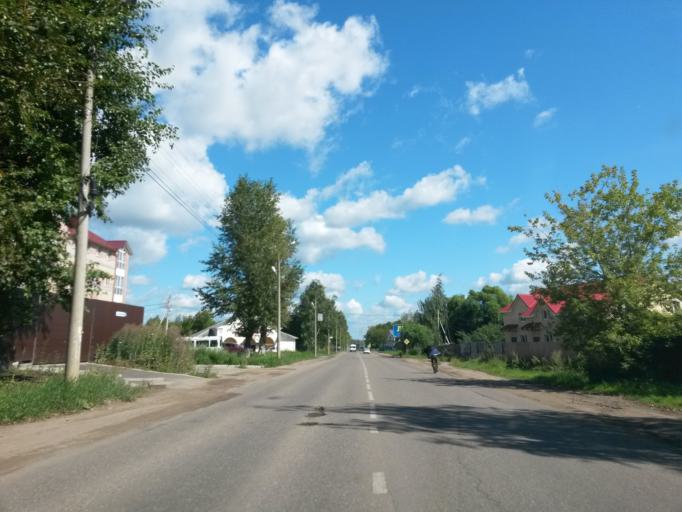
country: RU
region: Jaroslavl
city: Yaroslavl
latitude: 57.5806
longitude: 39.8706
